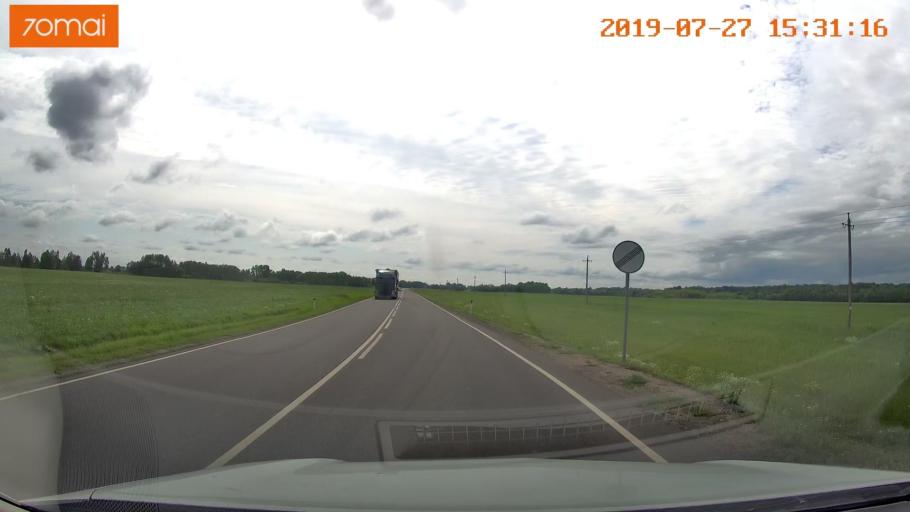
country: RU
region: Kaliningrad
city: Nesterov
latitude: 54.6247
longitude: 22.4947
